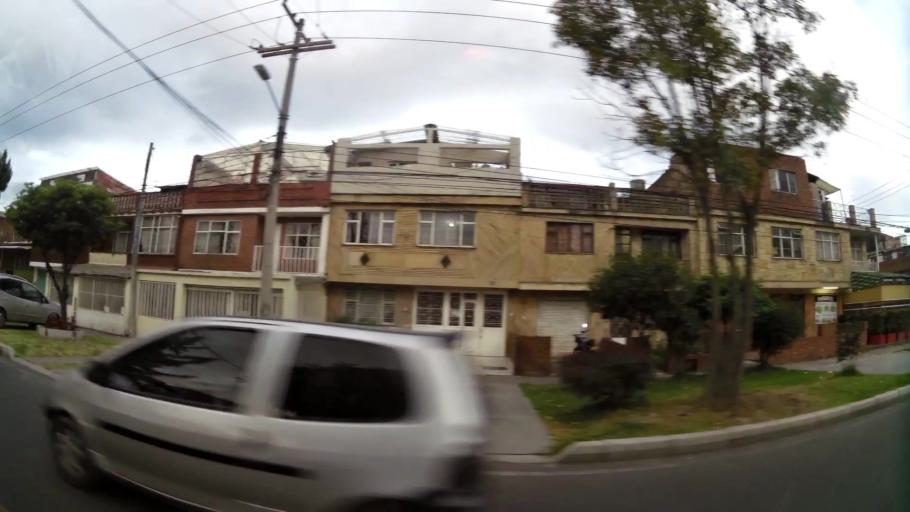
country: CO
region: Bogota D.C.
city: Bogota
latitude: 4.5955
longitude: -74.1302
